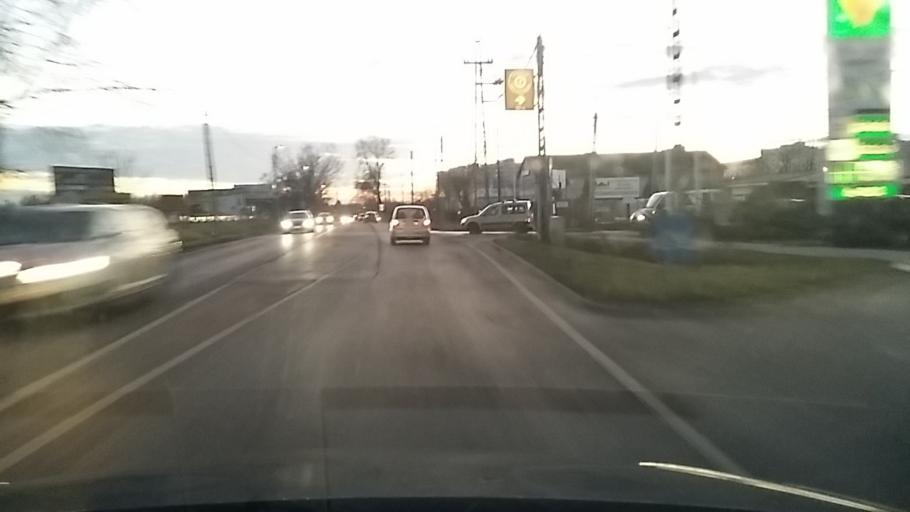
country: HU
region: Budapest
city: Budapest XV. keruelet
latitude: 47.5698
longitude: 19.1361
